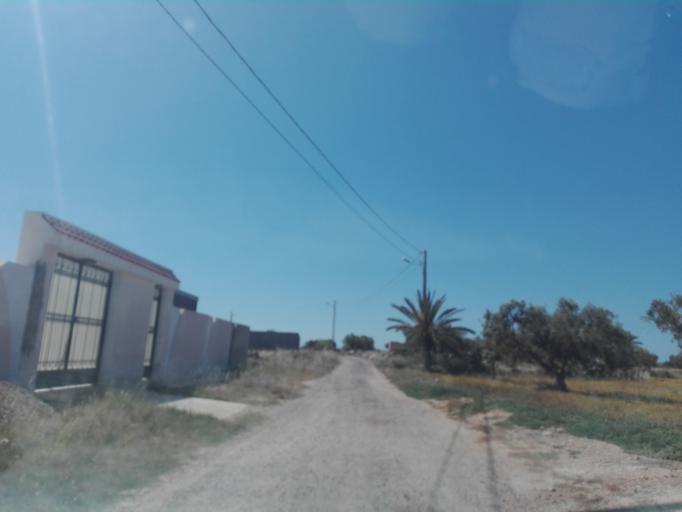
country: TN
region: Safaqis
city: Jabinyanah
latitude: 34.7187
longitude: 11.2428
